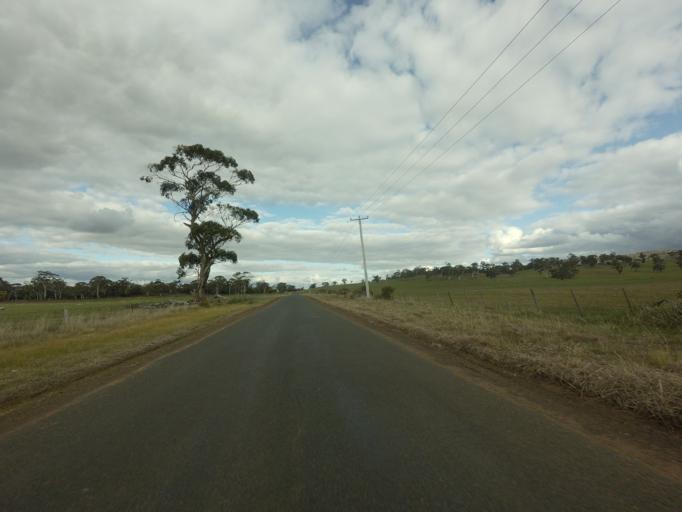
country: AU
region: Tasmania
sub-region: Northern Midlands
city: Evandale
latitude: -41.8697
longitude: 147.2933
